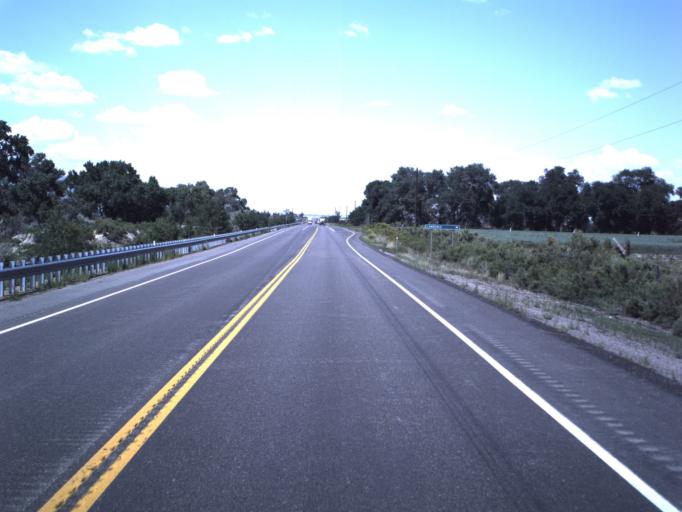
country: US
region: Utah
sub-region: Emery County
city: Huntington
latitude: 39.3021
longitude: -110.9642
